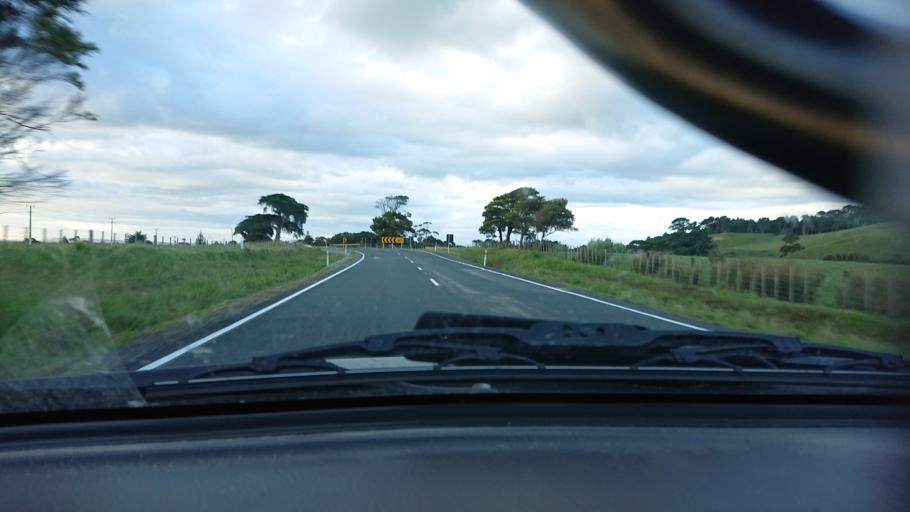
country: NZ
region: Auckland
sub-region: Auckland
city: Wellsford
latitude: -36.4564
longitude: 174.4393
